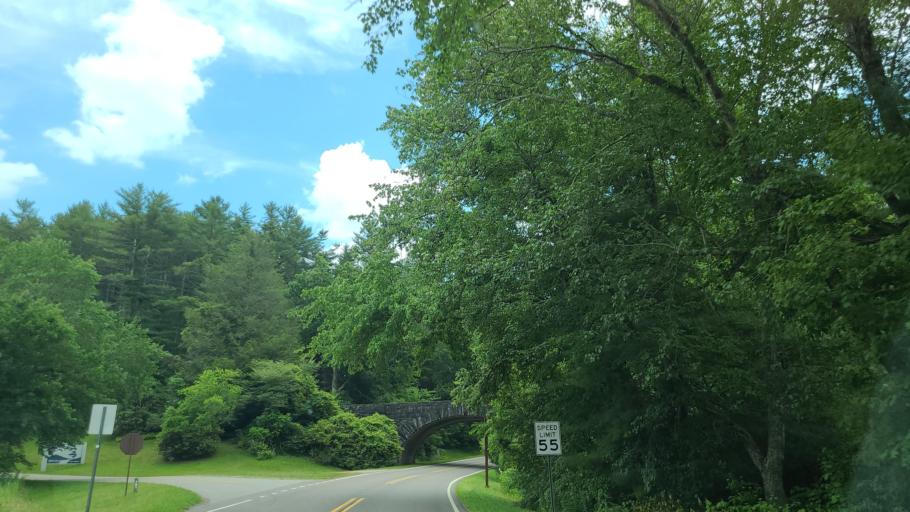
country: US
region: North Carolina
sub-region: Wilkes County
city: Mulberry
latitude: 36.3917
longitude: -81.2458
